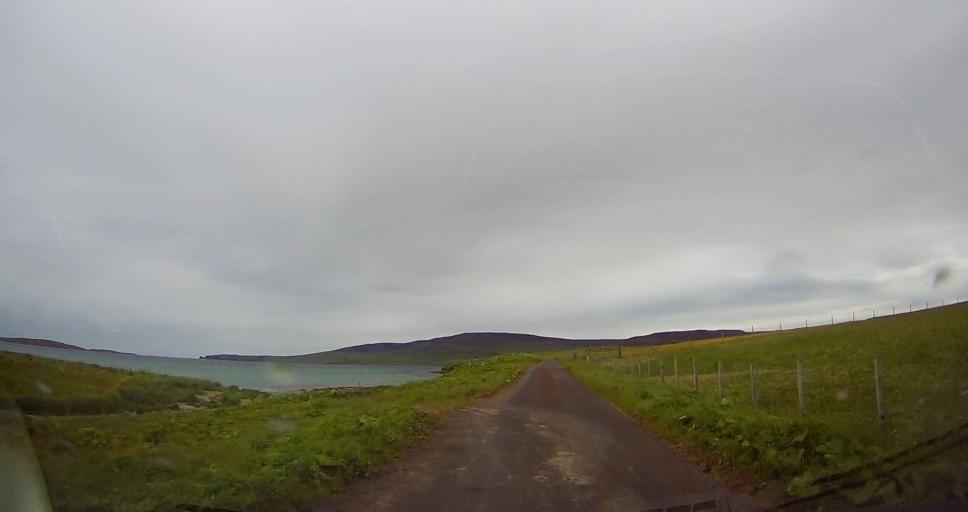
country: GB
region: Scotland
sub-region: Orkney Islands
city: Orkney
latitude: 59.1190
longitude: -3.0861
